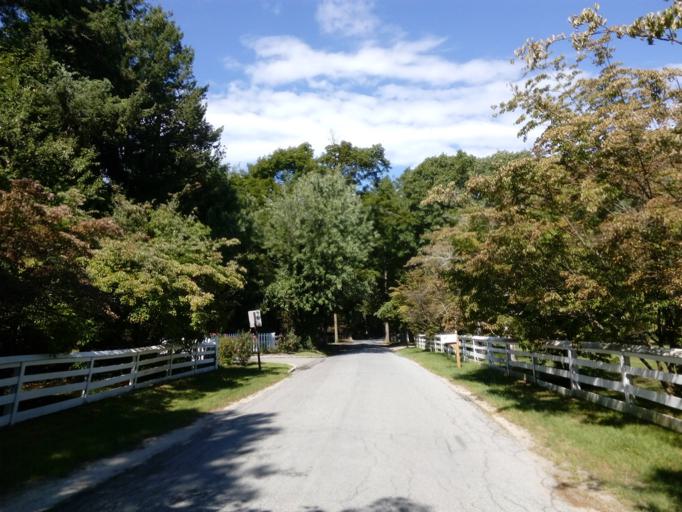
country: US
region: New York
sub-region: Nassau County
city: Laurel Hollow
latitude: 40.8649
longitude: -73.4767
